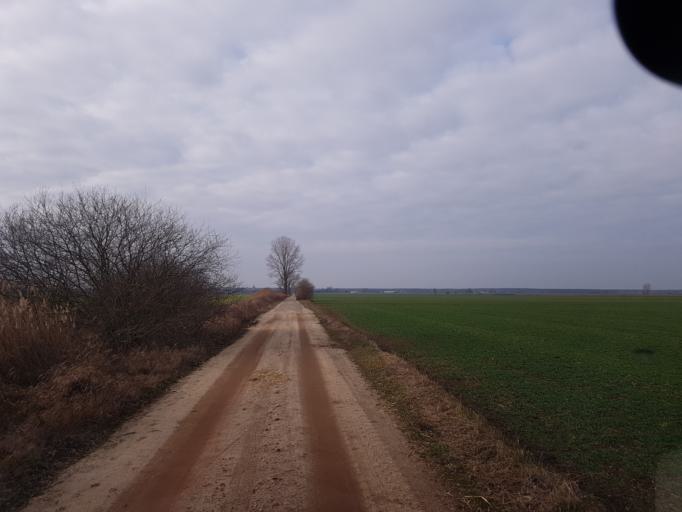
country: DE
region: Brandenburg
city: Doberlug-Kirchhain
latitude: 51.6651
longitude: 13.5586
